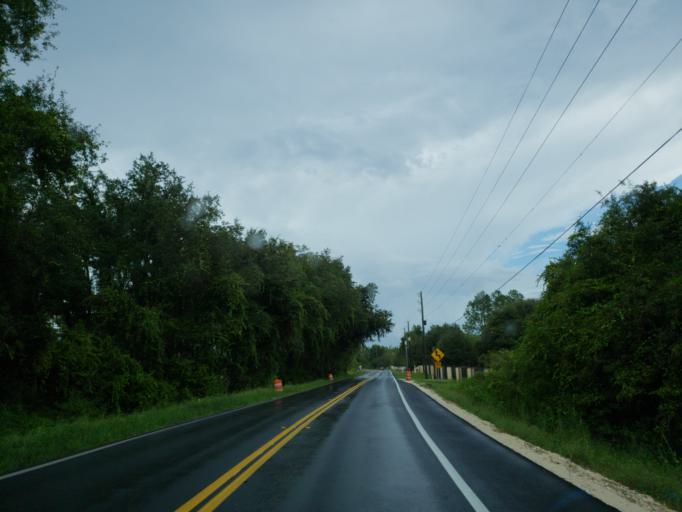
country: US
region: Florida
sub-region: Pasco County
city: Land O' Lakes
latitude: 28.3023
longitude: -82.4305
